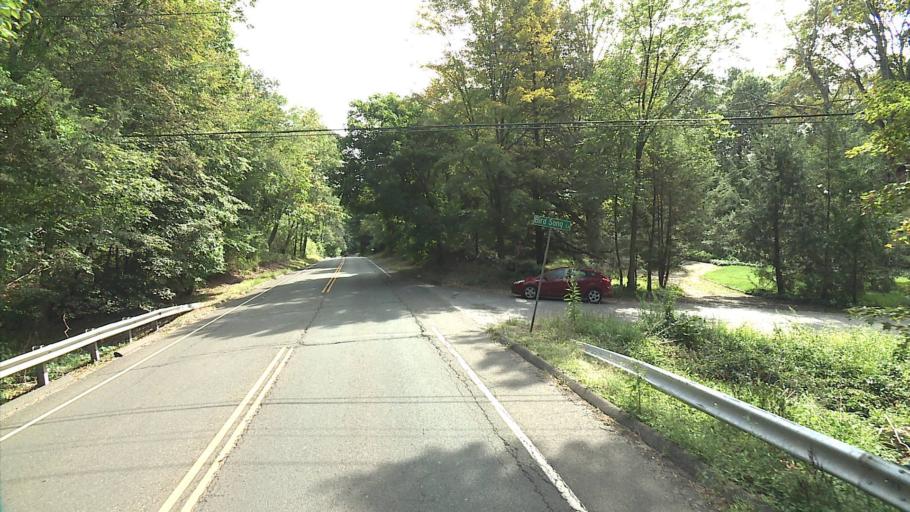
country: US
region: Connecticut
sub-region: Fairfield County
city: North Stamford
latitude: 41.1316
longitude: -73.5454
